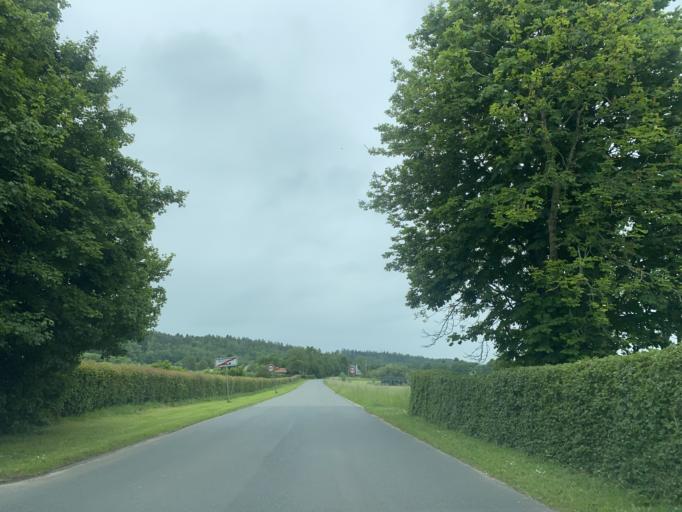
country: DK
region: Central Jutland
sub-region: Viborg Kommune
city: Bjerringbro
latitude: 56.3641
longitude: 9.6550
